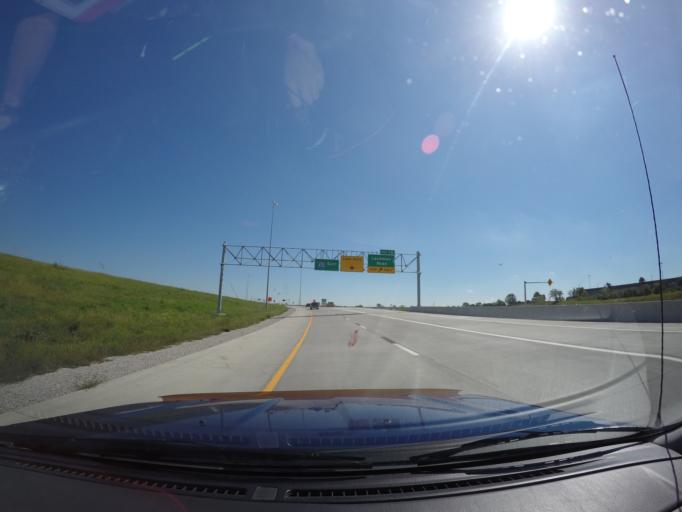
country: US
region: Kansas
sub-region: Johnson County
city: Lenexa
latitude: 38.9427
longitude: -94.7684
